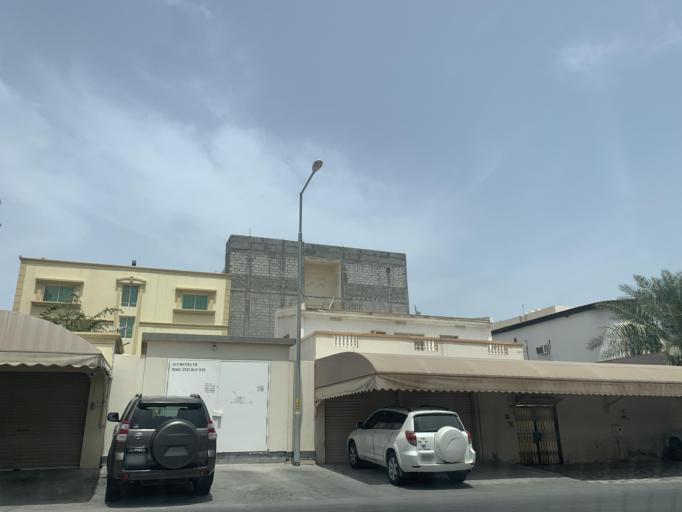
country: BH
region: Northern
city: Ar Rifa'
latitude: 26.1362
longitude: 50.5733
